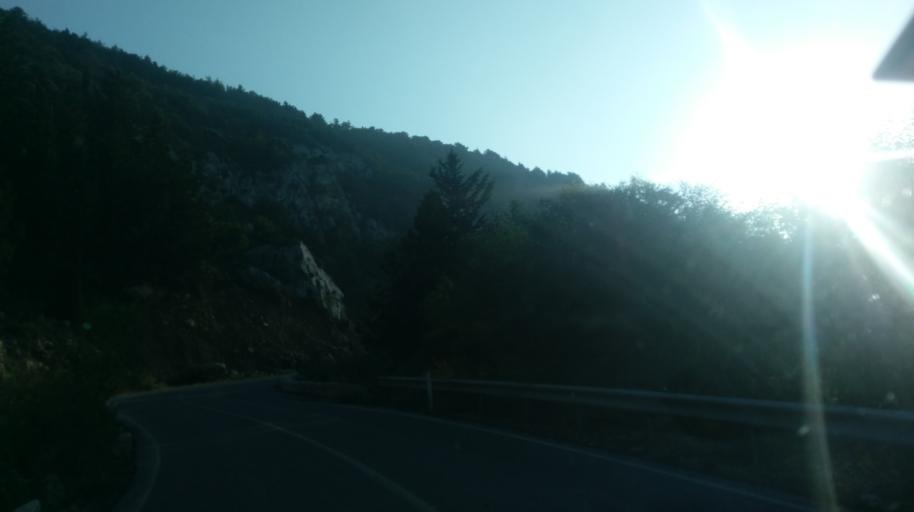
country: CY
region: Ammochostos
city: Trikomo
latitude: 35.3995
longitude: 33.9024
